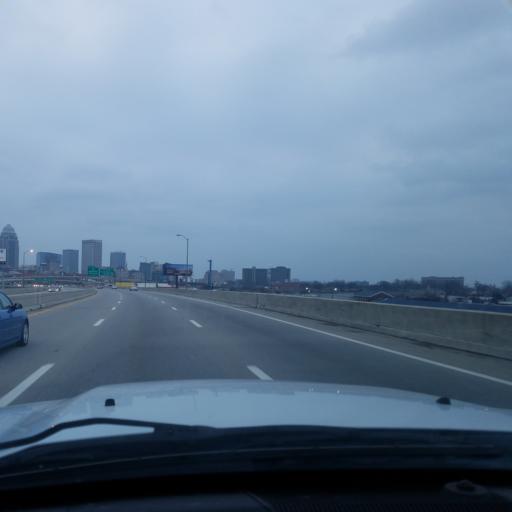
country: US
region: Kentucky
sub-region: Jefferson County
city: Louisville
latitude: 38.2625
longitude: -85.7722
